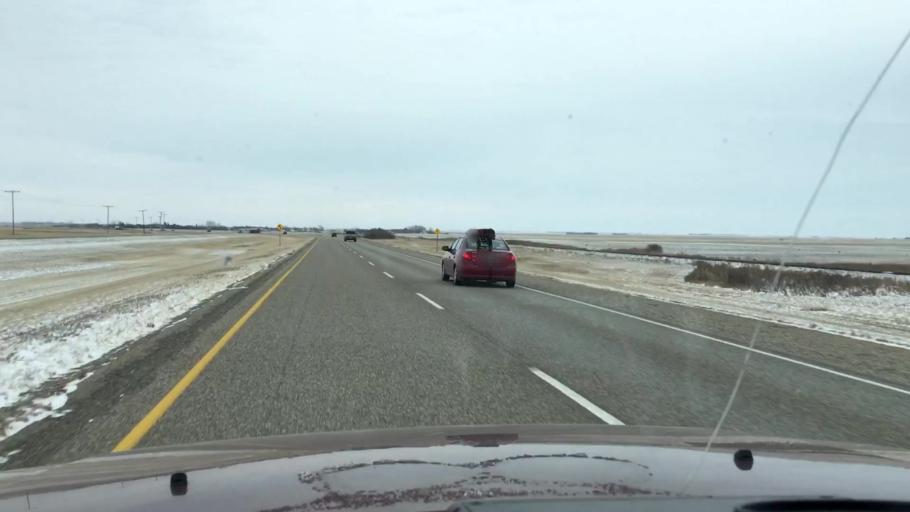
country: CA
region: Saskatchewan
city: Watrous
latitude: 51.1752
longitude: -105.9345
